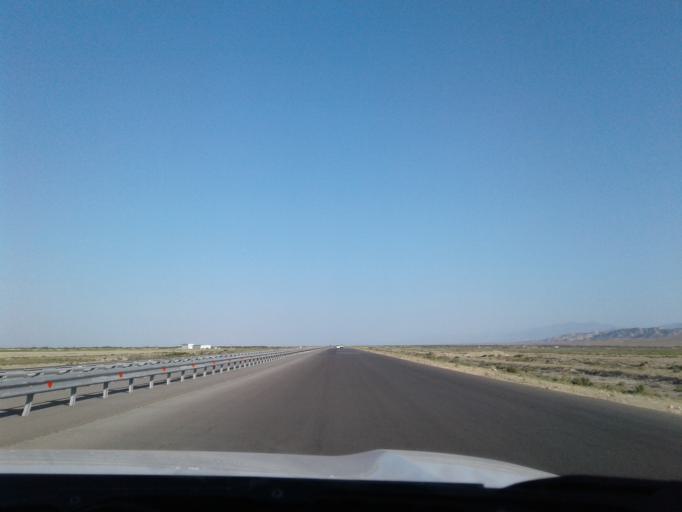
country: TM
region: Balkan
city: Serdar
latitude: 38.9349
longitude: 56.4406
